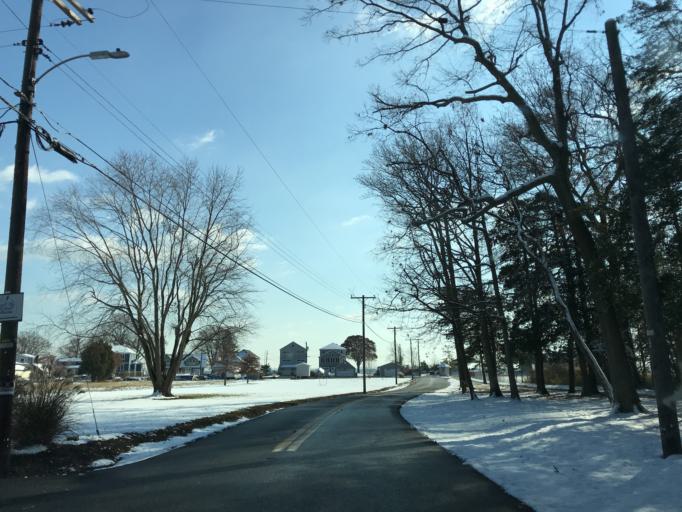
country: US
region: Maryland
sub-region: Baltimore County
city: Bowleys Quarters
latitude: 39.3083
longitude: -76.3713
